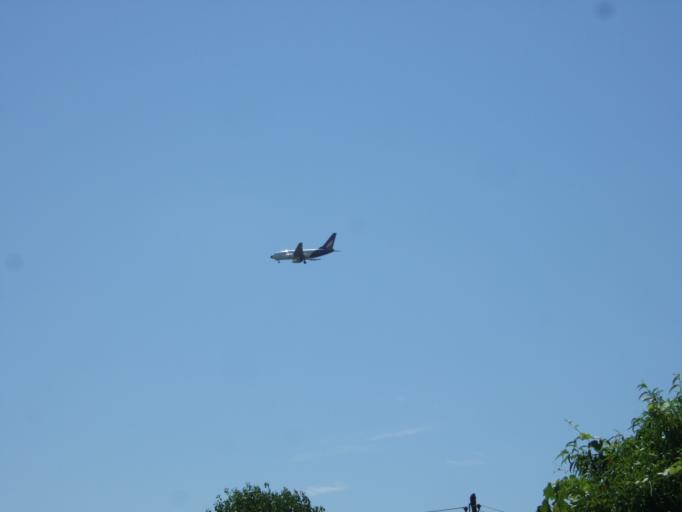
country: AL
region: Durres
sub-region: Rrethi i Krujes
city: Fushe-Kruje
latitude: 41.4566
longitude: 19.7259
